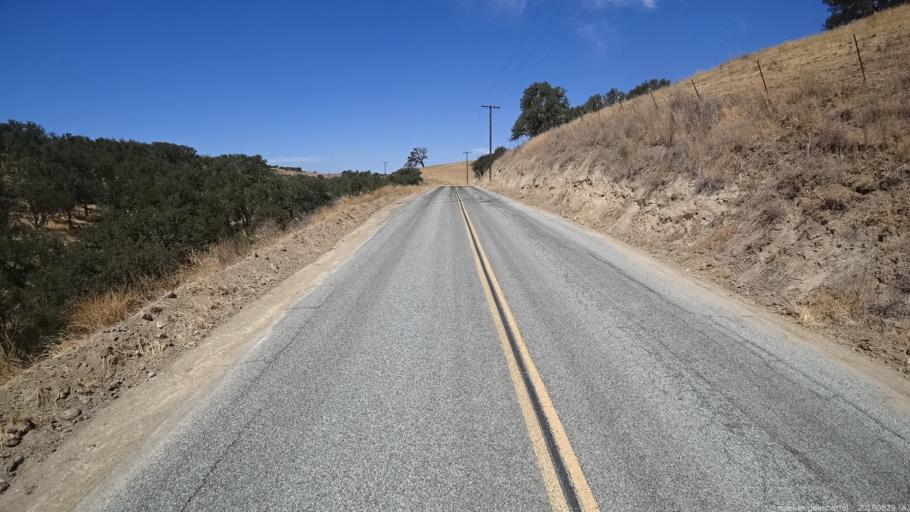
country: US
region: California
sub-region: San Luis Obispo County
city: Lake Nacimiento
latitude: 35.8247
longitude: -120.8421
